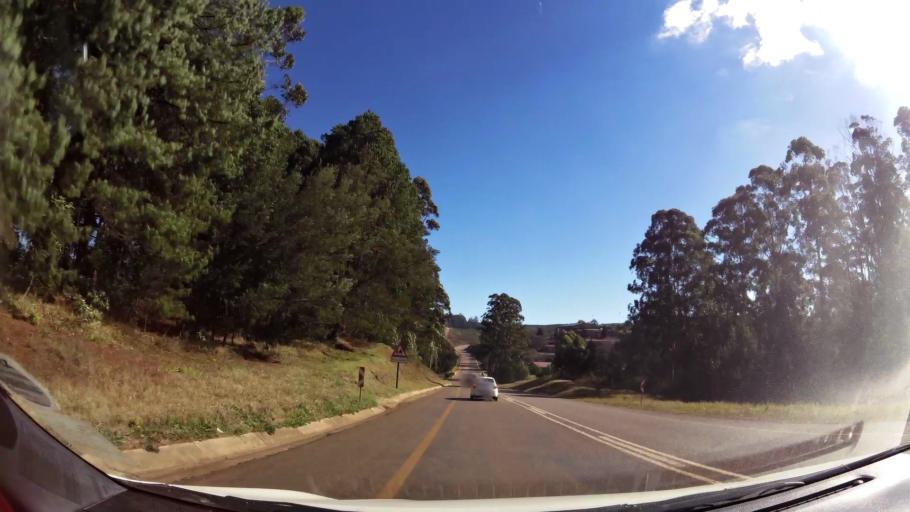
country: ZA
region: Limpopo
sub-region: Capricorn District Municipality
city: Mankoeng
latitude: -23.9096
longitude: 29.9785
